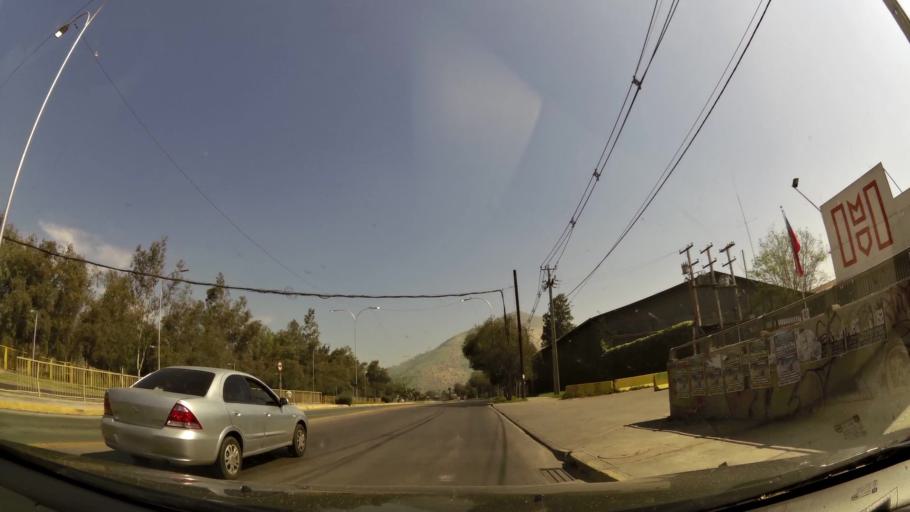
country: CL
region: Santiago Metropolitan
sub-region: Provincia de Santiago
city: Lo Prado
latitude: -33.4011
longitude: -70.6914
